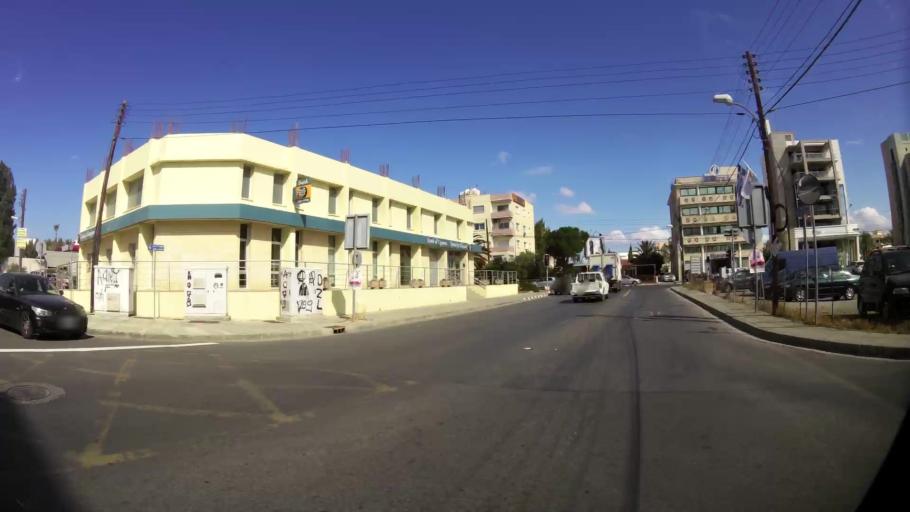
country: CY
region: Lefkosia
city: Nicosia
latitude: 35.1415
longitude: 33.3694
